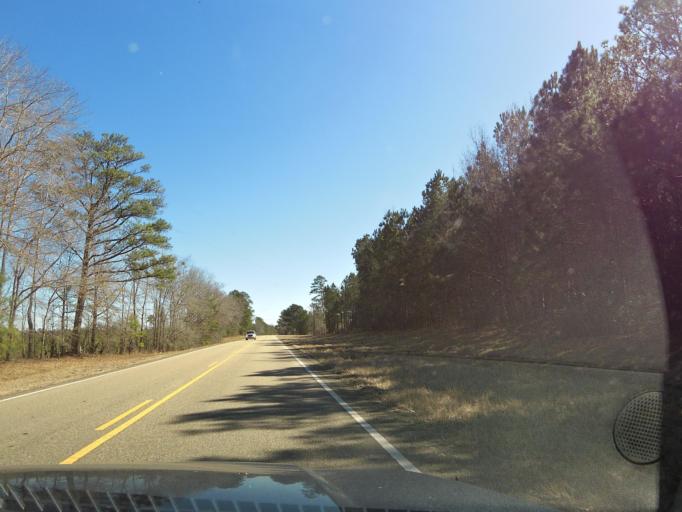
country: US
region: Alabama
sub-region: Montgomery County
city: Pike Road
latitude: 32.1692
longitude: -86.0691
